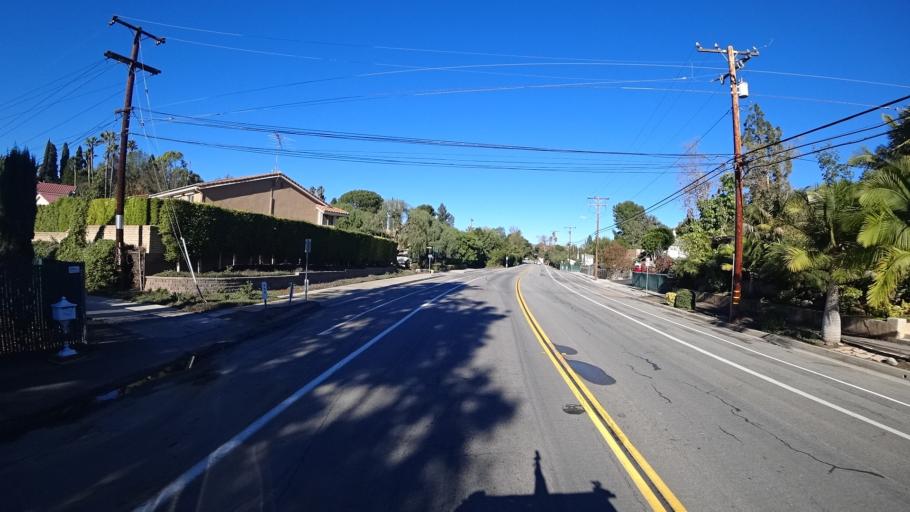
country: US
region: California
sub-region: Orange County
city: Yorba Linda
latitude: 33.8778
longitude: -117.8015
